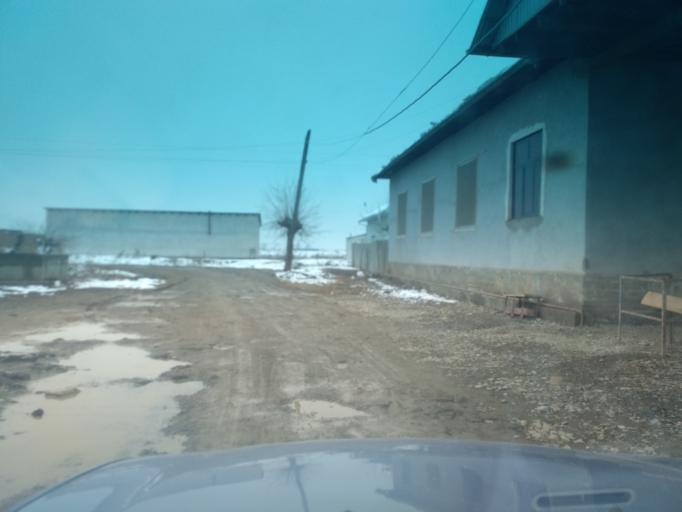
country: UZ
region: Sirdaryo
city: Guliston
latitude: 40.4790
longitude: 68.7493
